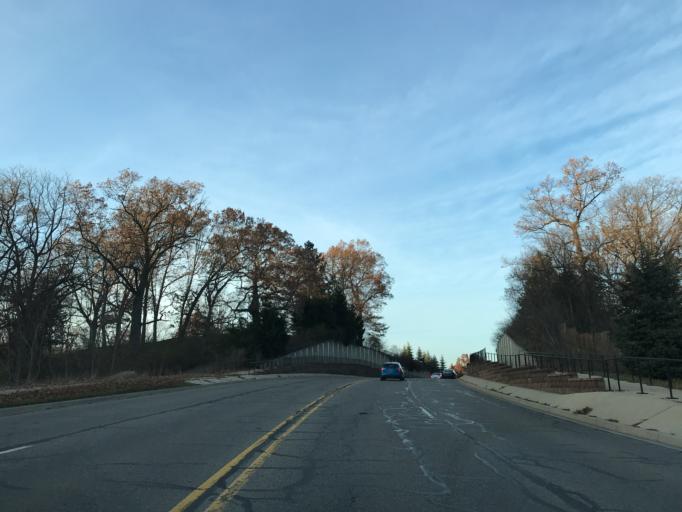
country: US
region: Michigan
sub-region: Washtenaw County
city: Ann Arbor
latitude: 42.2671
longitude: -83.6974
